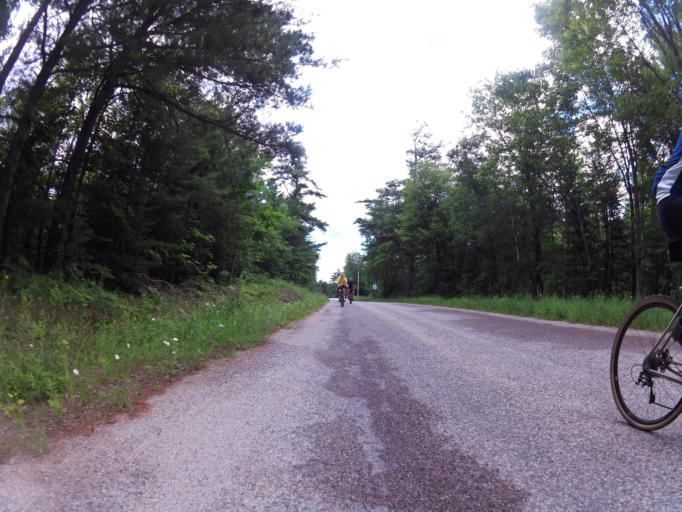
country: CA
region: Ontario
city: Renfrew
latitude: 45.0390
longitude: -76.7124
